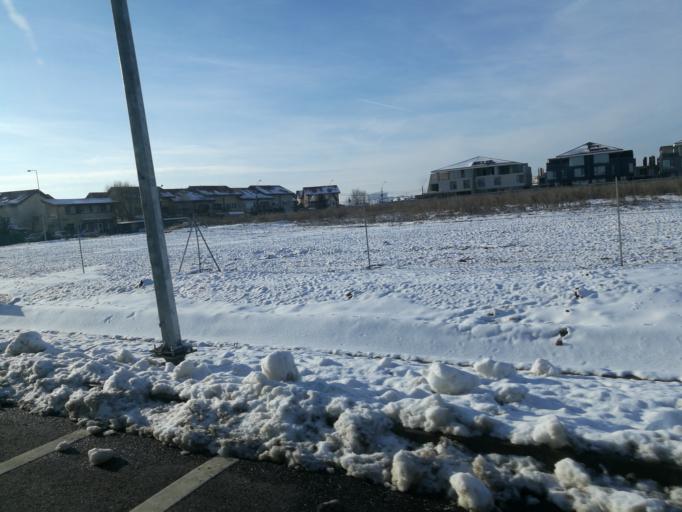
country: RO
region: Ilfov
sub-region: Voluntari City
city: Voluntari
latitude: 44.4935
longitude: 26.1494
